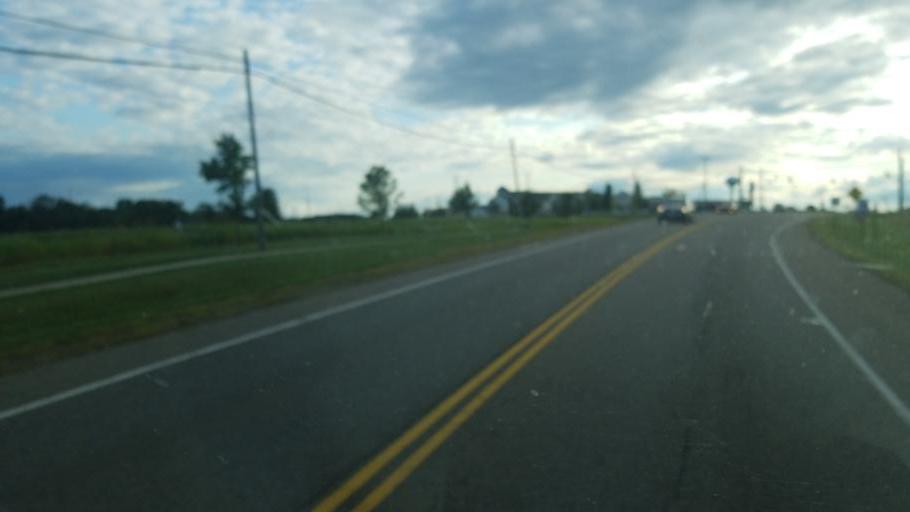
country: US
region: Ohio
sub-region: Knox County
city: Gambier
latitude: 40.4036
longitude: -82.4356
